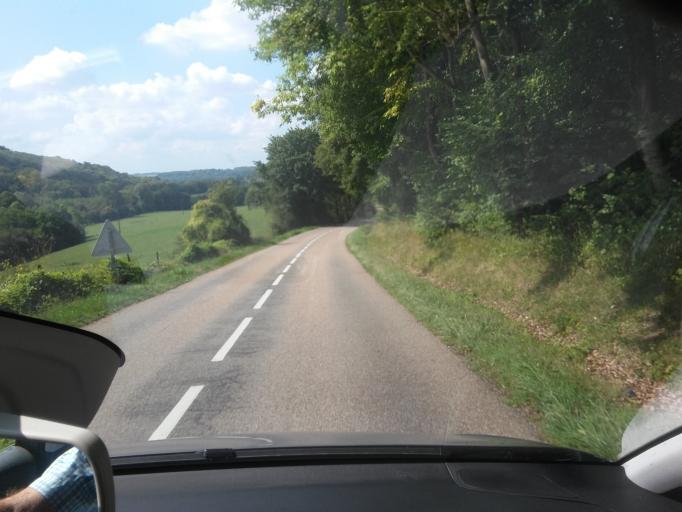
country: BE
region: Wallonia
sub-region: Province du Luxembourg
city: Rouvroy
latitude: 49.4976
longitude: 5.5496
